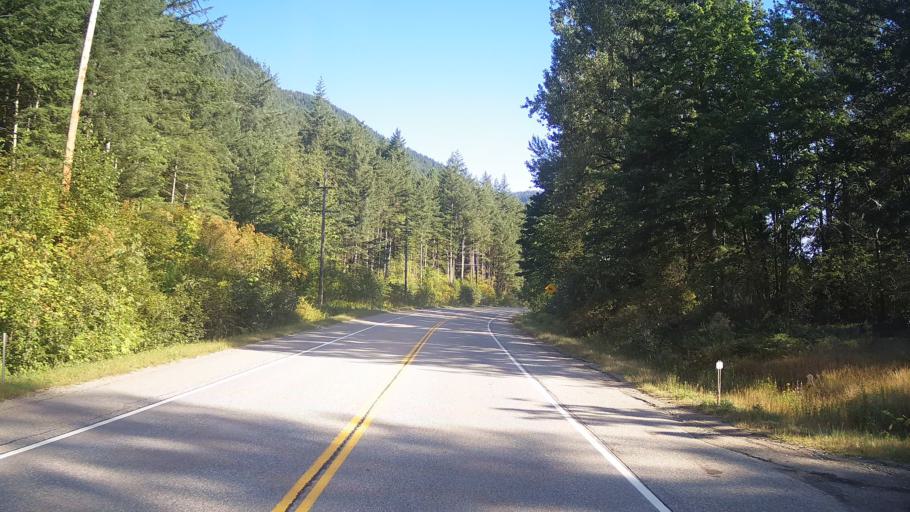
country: CA
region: British Columbia
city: Hope
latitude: 49.4321
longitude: -121.4389
